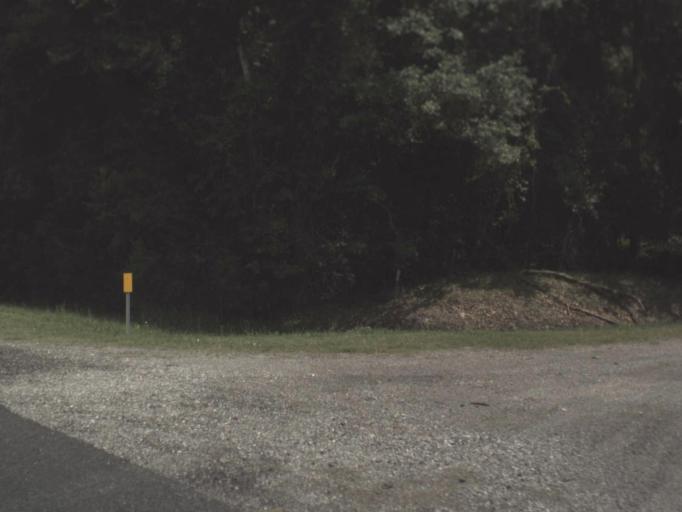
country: US
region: Florida
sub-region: Alachua County
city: Waldo
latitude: 29.7651
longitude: -82.1462
